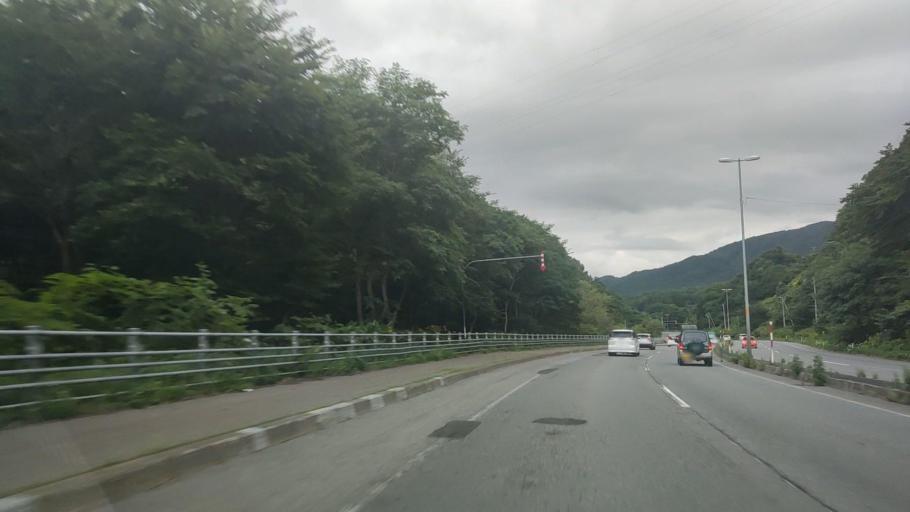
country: JP
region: Hokkaido
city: Nanae
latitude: 41.9382
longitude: 140.6420
